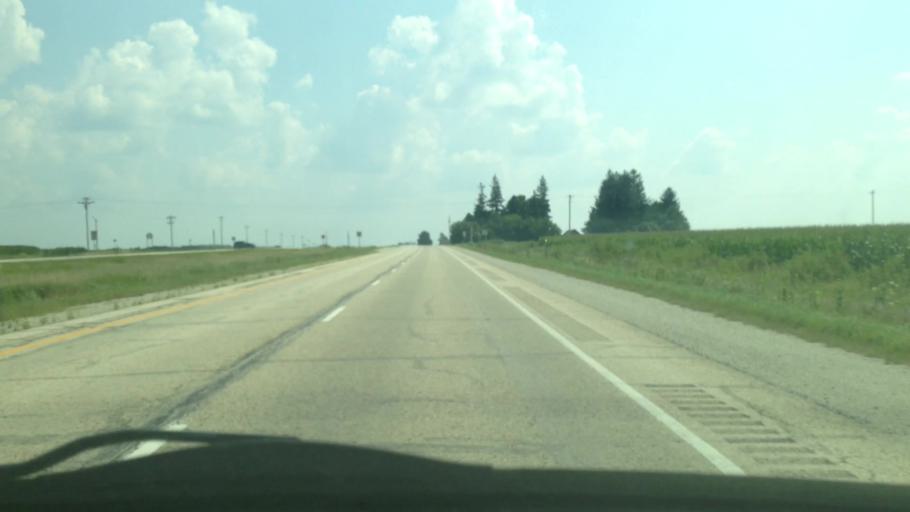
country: US
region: Iowa
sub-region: Bremer County
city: Tripoli
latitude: 42.8788
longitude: -92.3377
